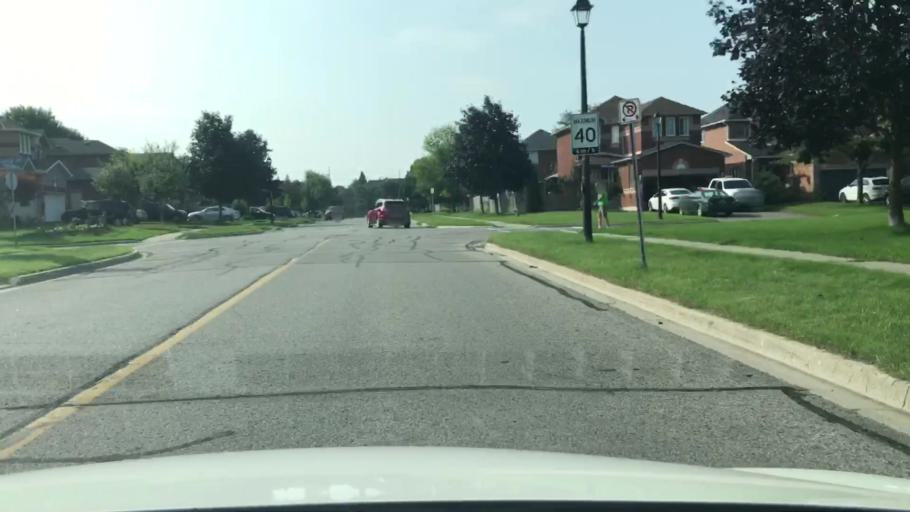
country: CA
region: Ontario
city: Newmarket
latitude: 44.0469
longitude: -79.4474
